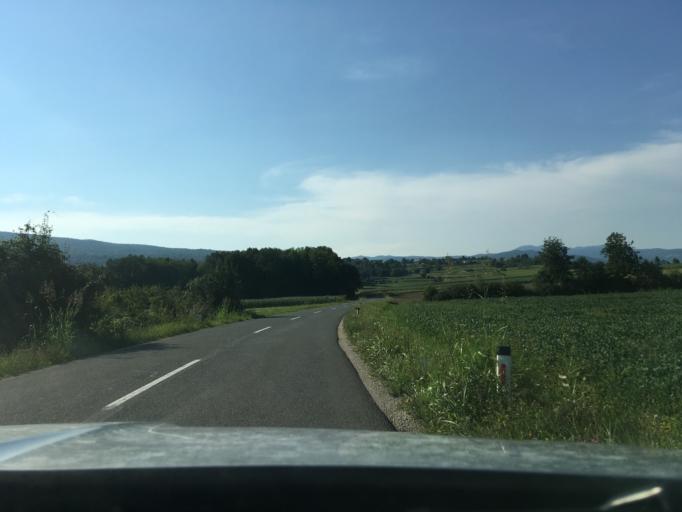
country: SI
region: Crnomelj
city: Crnomelj
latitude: 45.5232
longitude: 15.1665
